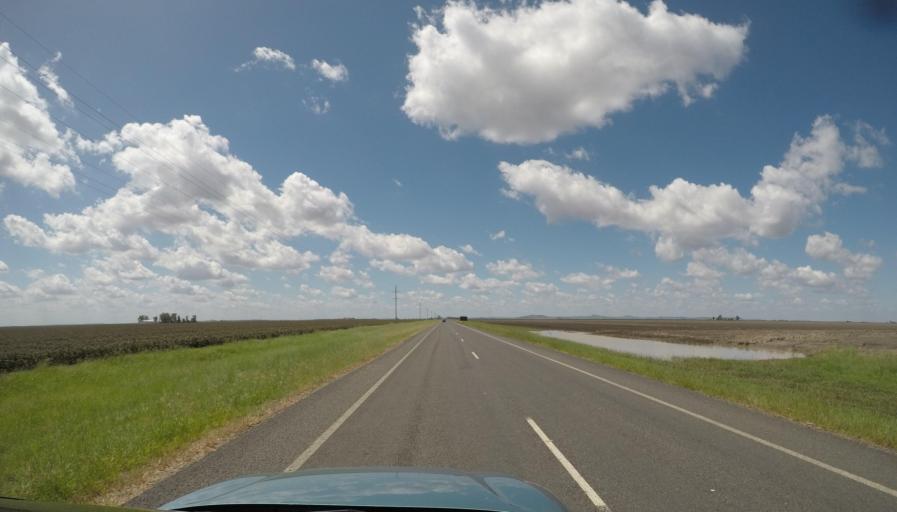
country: AU
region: Queensland
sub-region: Toowoomba
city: Oakey
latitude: -27.5155
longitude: 151.3942
